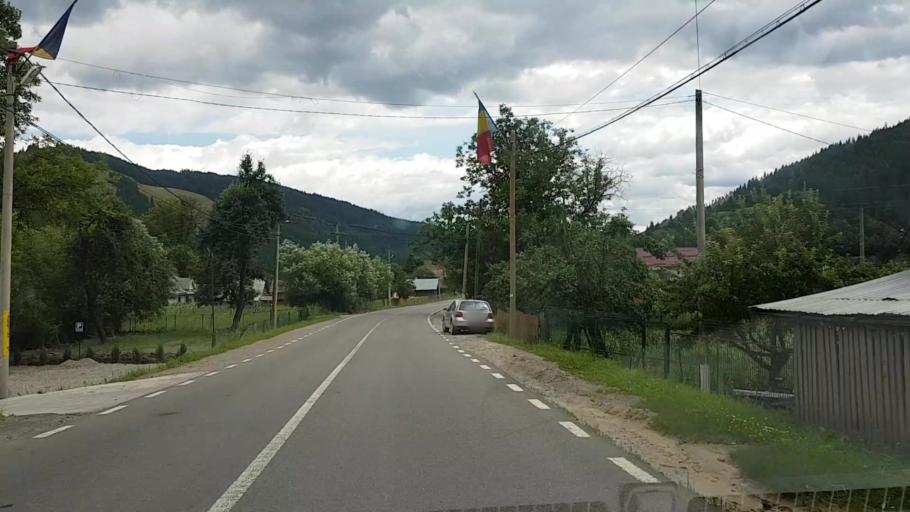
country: RO
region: Neamt
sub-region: Comuna Poiana Teiului
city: Poiana Teiului
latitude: 47.1172
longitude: 25.9192
